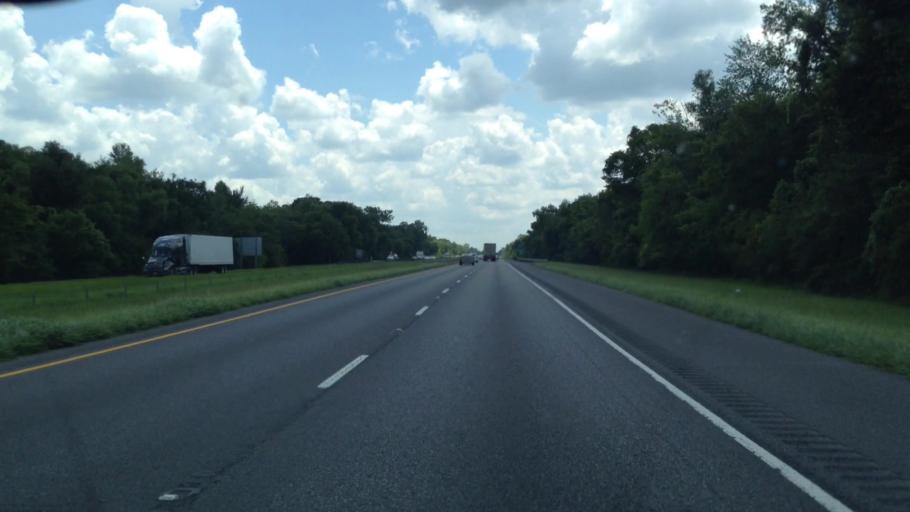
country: US
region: Louisiana
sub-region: Saint James Parish
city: Grand Point
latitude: 30.1447
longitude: -90.7632
